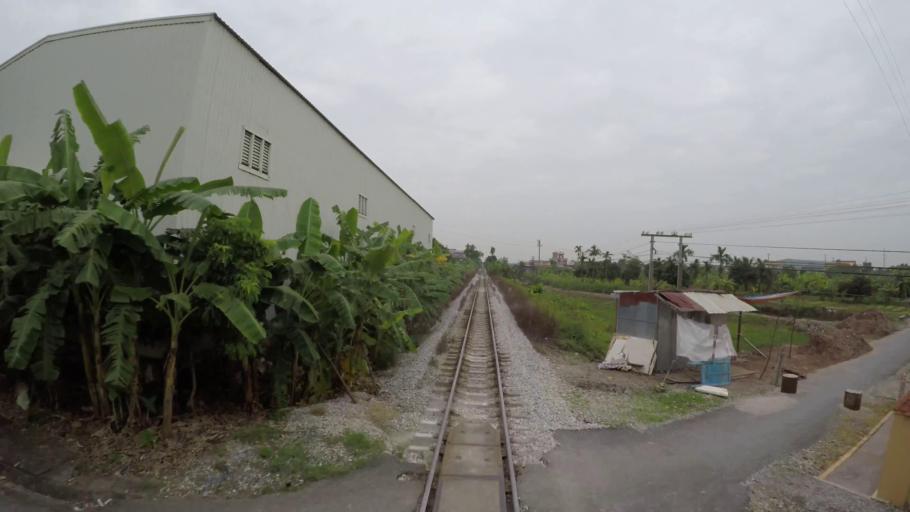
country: VN
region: Hai Phong
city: An Duong
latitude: 20.8978
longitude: 106.5822
